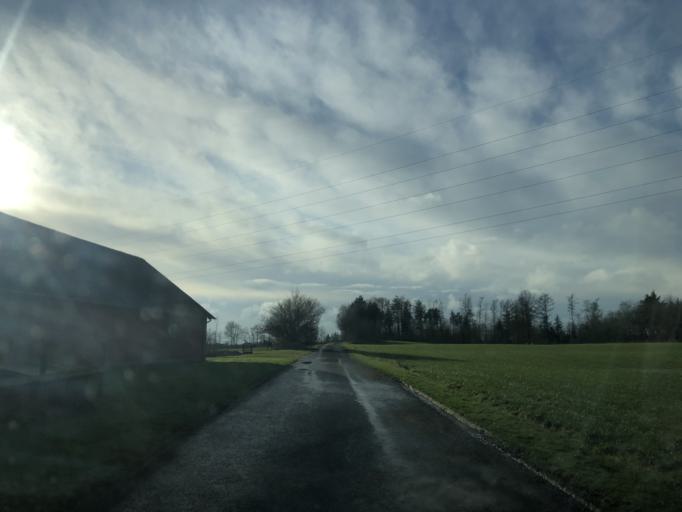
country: DK
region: North Denmark
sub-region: Vesthimmerland Kommune
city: Alestrup
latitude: 56.6391
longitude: 9.6152
